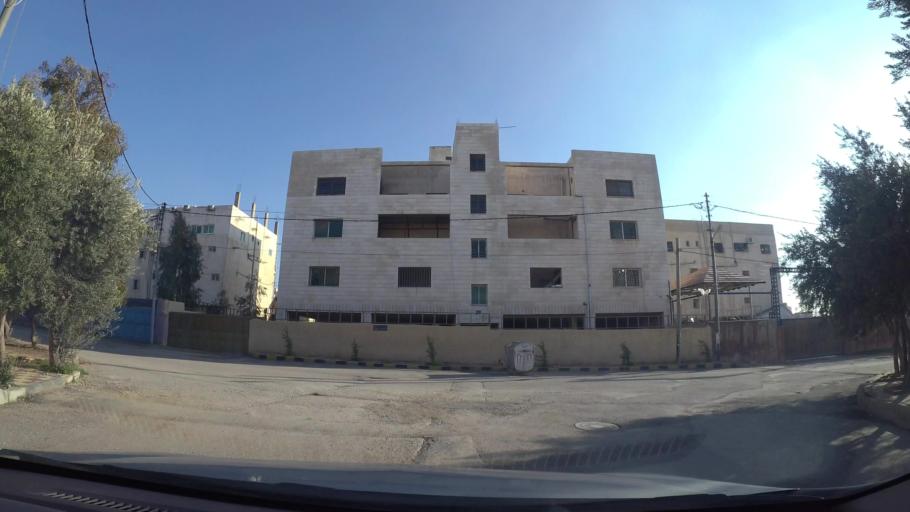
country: JO
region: Amman
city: Al Bunayyat ash Shamaliyah
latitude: 31.8967
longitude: 35.9108
